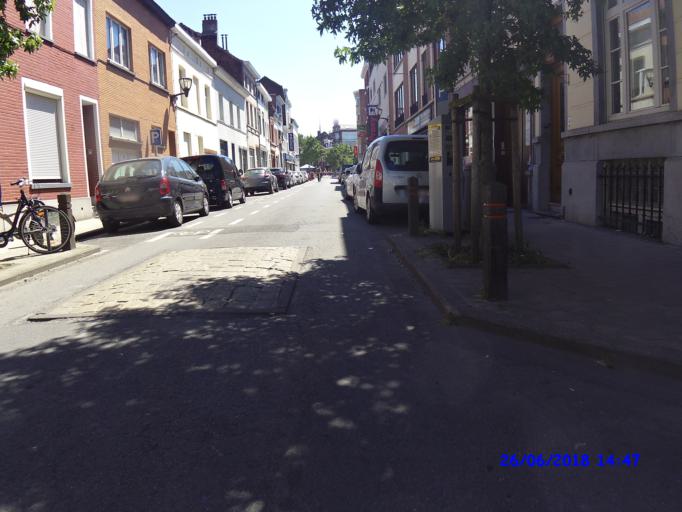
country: BE
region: Brussels Capital
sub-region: Bruxelles-Capitale
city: Brussels
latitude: 50.8742
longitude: 4.3254
